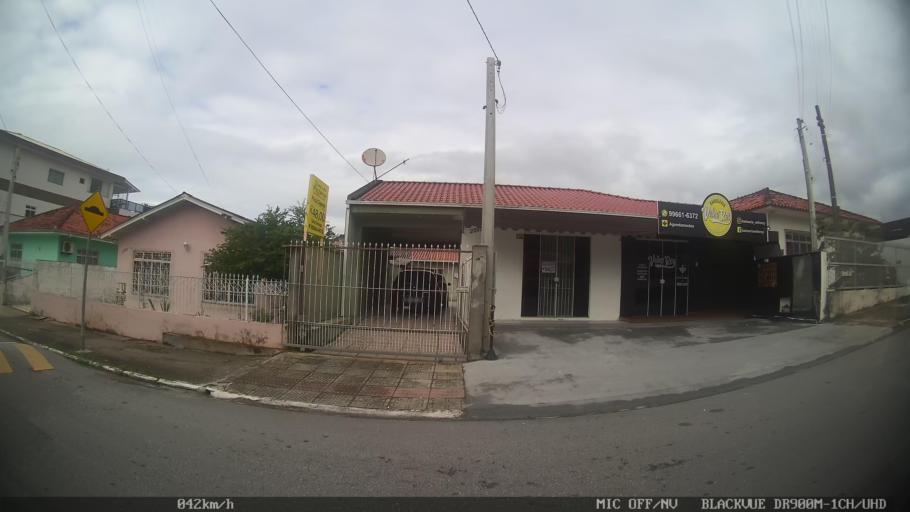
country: BR
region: Santa Catarina
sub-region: Sao Jose
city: Campinas
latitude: -27.5617
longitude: -48.6333
